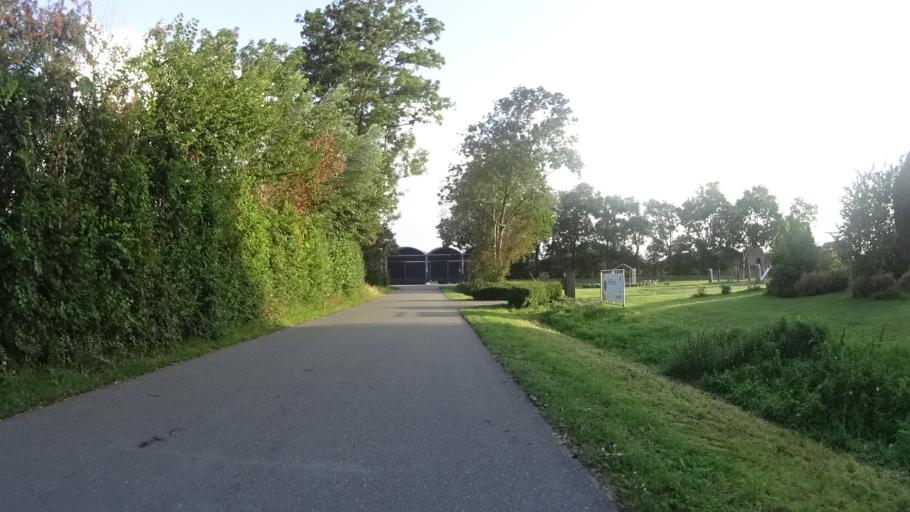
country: NL
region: Zeeland
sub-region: Gemeente Middelburg
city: Middelburg
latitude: 51.5222
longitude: 3.6264
